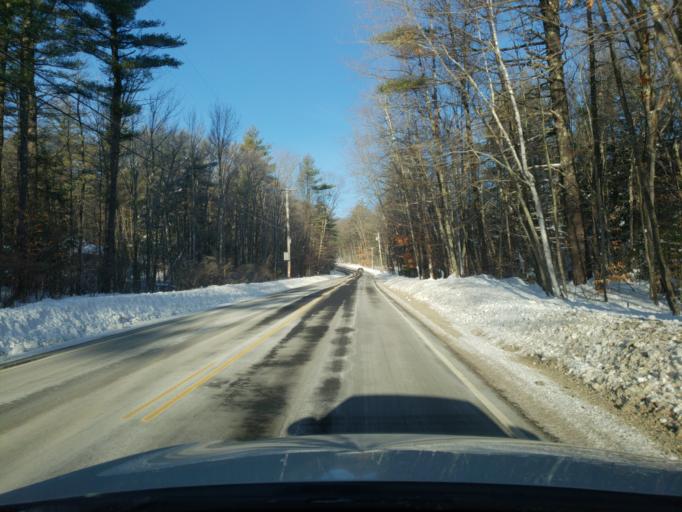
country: US
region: New Hampshire
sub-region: Hillsborough County
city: Greenfield
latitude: 42.9979
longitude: -71.8256
